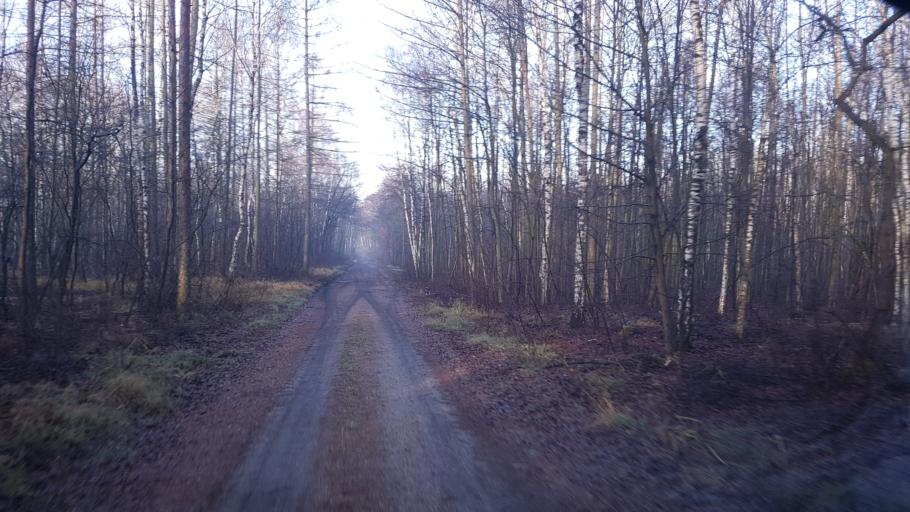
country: DE
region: Brandenburg
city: Trobitz
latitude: 51.5845
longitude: 13.4490
